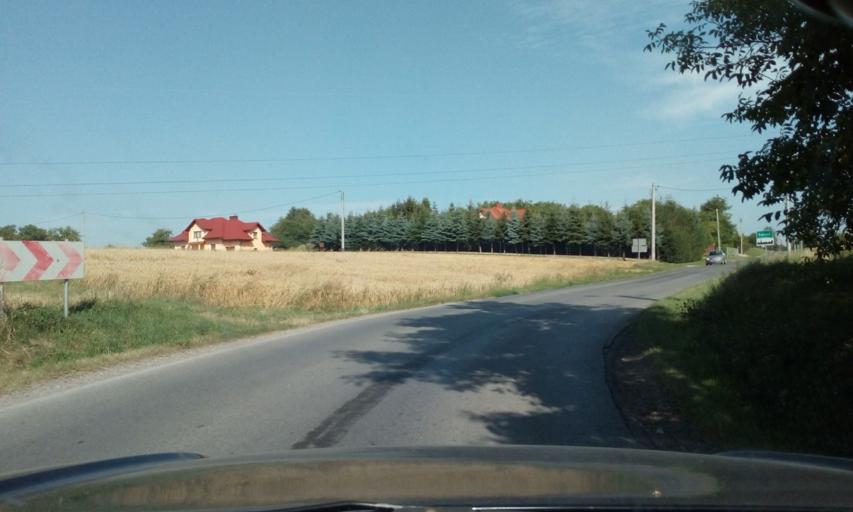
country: PL
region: Subcarpathian Voivodeship
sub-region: Powiat lancucki
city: Lancut
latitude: 50.0532
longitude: 22.2353
